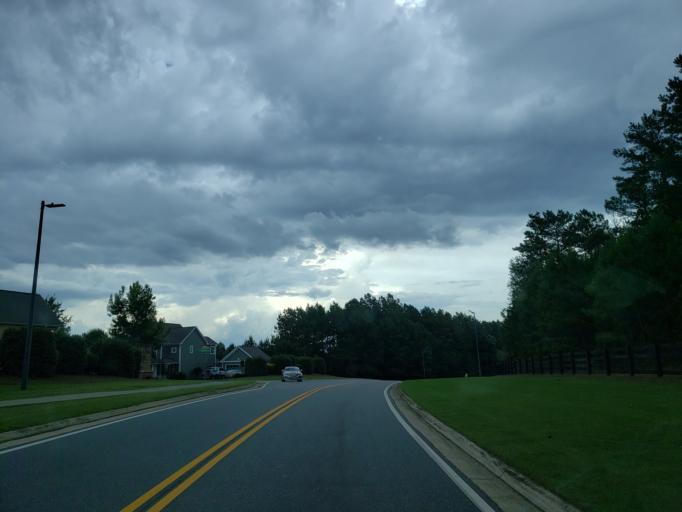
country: US
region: Georgia
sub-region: Paulding County
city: Dallas
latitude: 34.0199
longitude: -84.7937
